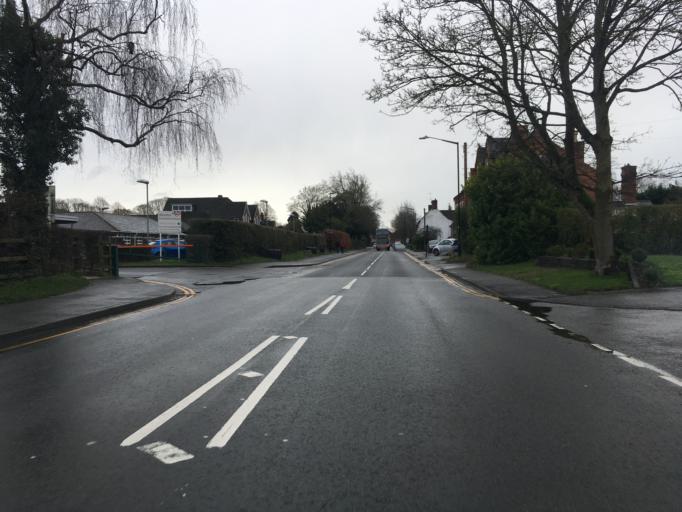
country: GB
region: England
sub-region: Warwickshire
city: Alcester
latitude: 52.2193
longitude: -1.8766
